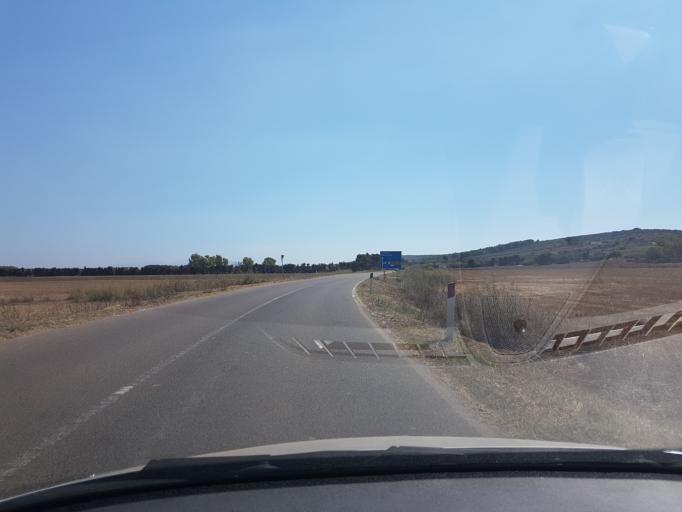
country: IT
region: Sardinia
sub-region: Provincia di Oristano
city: Cabras
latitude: 39.9624
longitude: 8.4540
